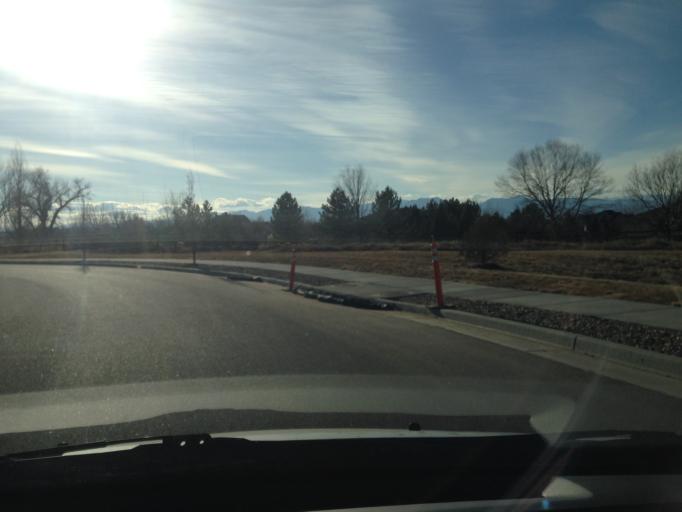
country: US
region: Colorado
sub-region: Boulder County
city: Erie
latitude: 40.0406
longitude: -105.0852
